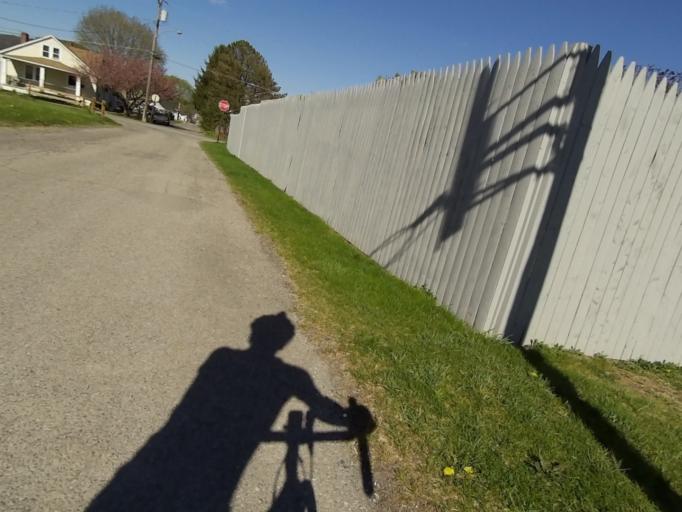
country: US
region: Pennsylvania
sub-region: Centre County
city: Bellefonte
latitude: 40.9097
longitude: -77.7878
